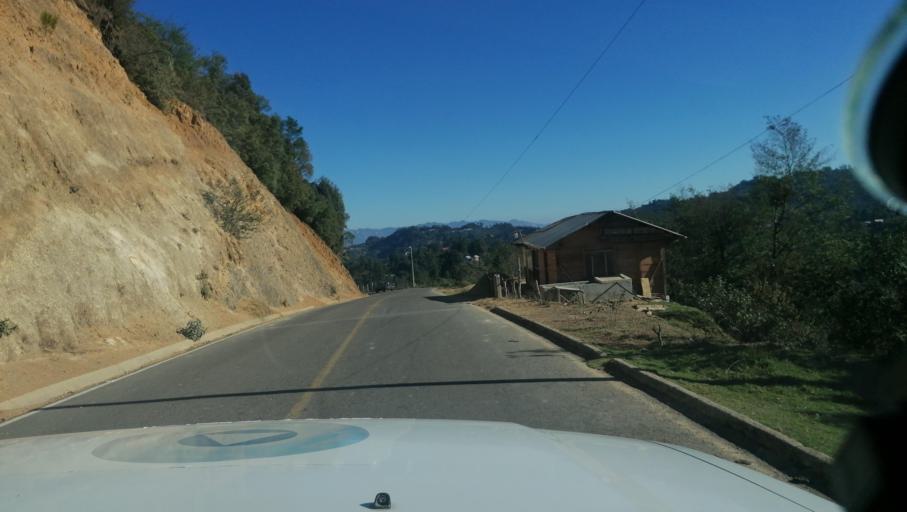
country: MX
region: Chiapas
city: Motozintla de Mendoza
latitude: 15.2420
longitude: -92.2302
